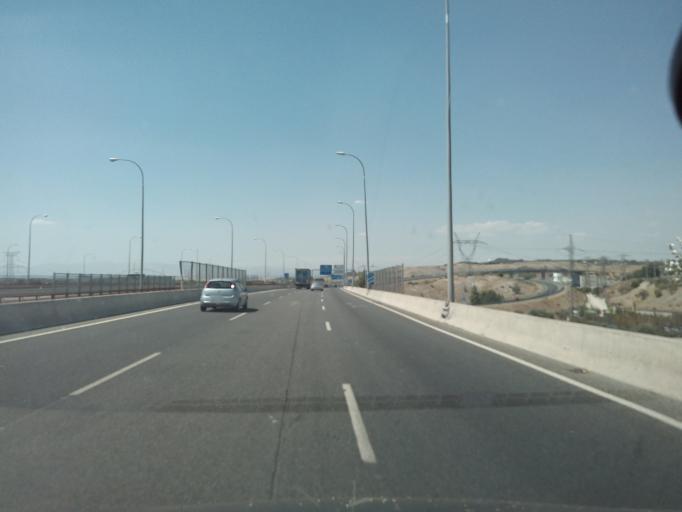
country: ES
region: Madrid
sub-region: Provincia de Madrid
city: San Fernando de Henares
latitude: 40.4462
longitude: -3.5158
